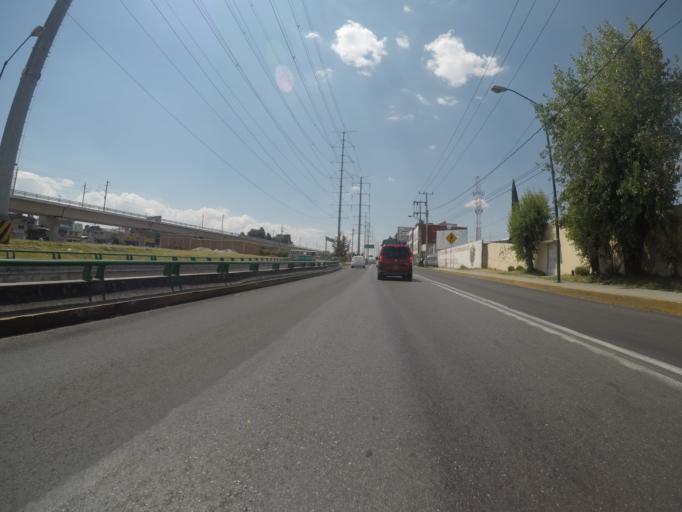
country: MX
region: Mexico
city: San Buenaventura
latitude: 19.2690
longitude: -99.6579
